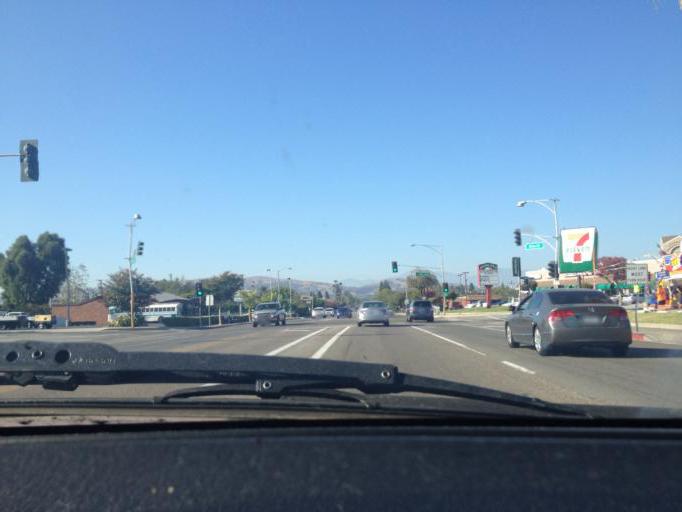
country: US
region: California
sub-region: Orange County
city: Brea
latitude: 33.9026
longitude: -117.9077
